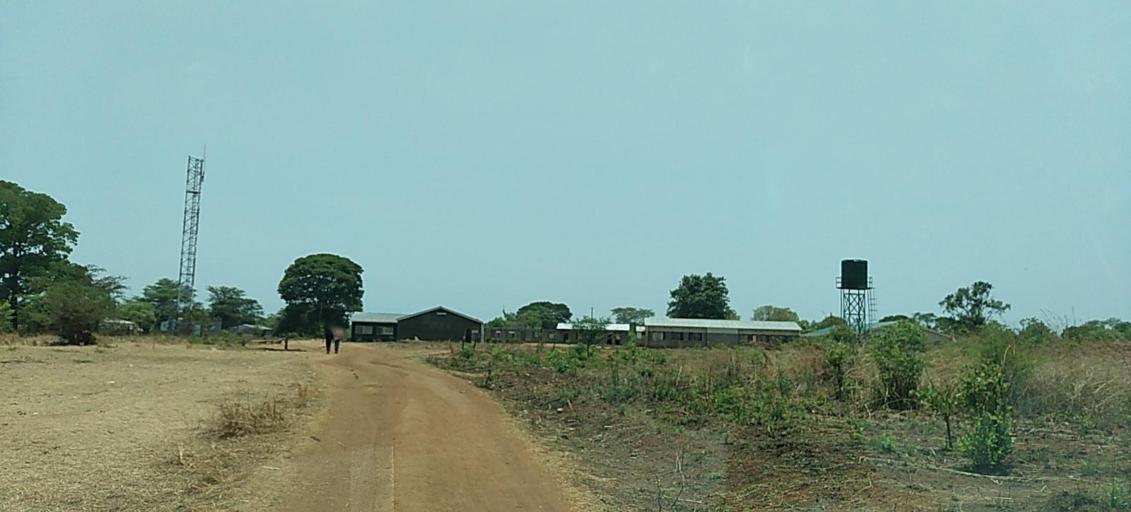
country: ZM
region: Copperbelt
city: Mpongwe
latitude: -13.8348
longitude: 27.8380
